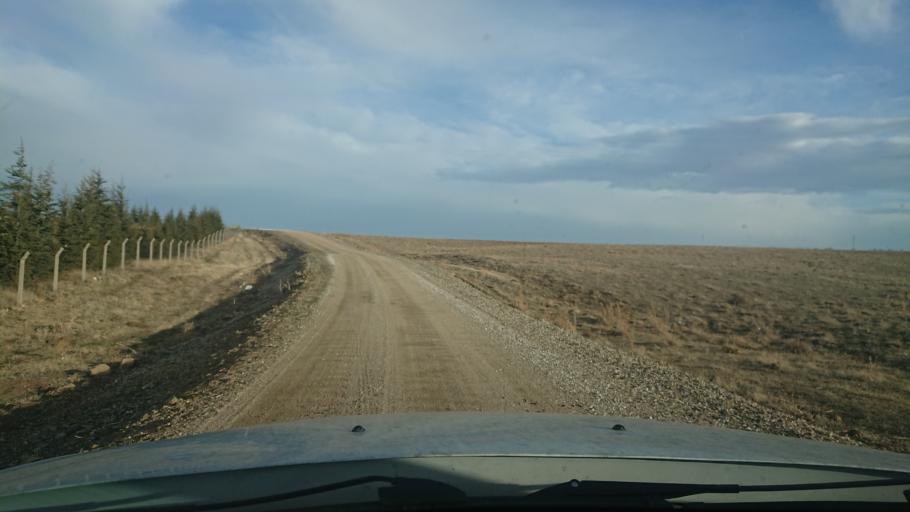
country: TR
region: Aksaray
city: Agacoren
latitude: 38.7148
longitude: 33.8690
